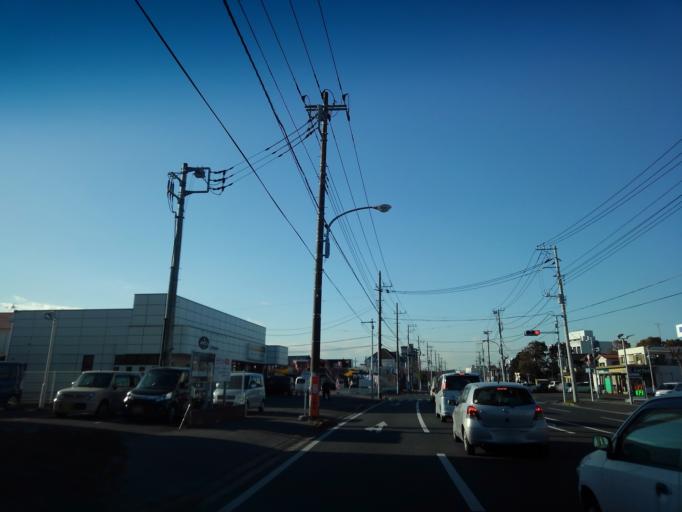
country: JP
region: Chiba
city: Kimitsu
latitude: 35.3268
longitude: 139.9062
